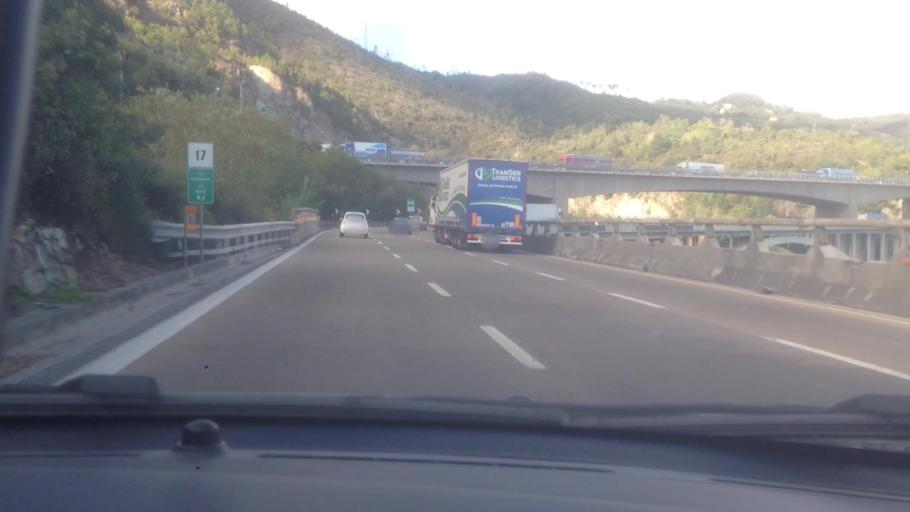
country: IT
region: Liguria
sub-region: Provincia di Genova
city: Arenzano
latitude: 44.4143
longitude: 8.7025
